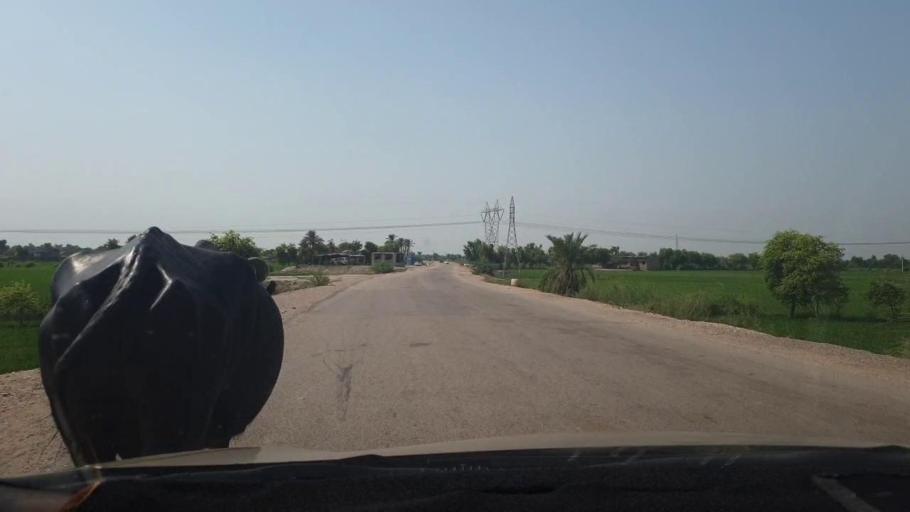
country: PK
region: Sindh
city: Larkana
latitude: 27.6059
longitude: 68.2410
